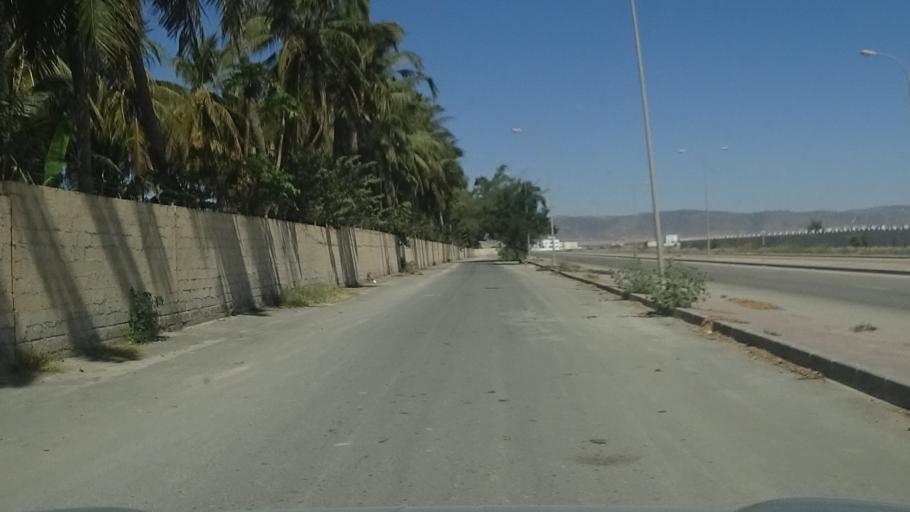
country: OM
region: Zufar
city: Salalah
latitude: 17.0273
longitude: 54.1236
